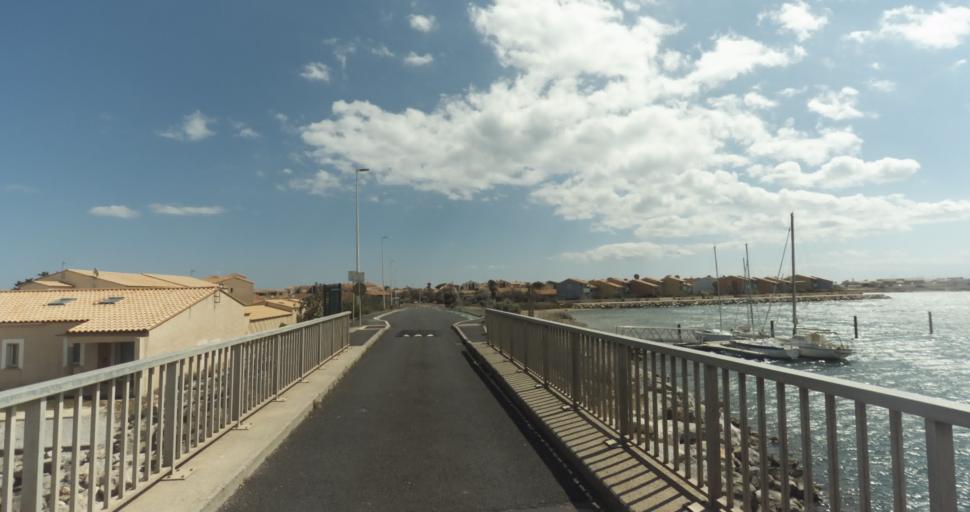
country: FR
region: Languedoc-Roussillon
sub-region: Departement de l'Aude
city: Leucate
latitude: 42.8778
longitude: 3.0451
